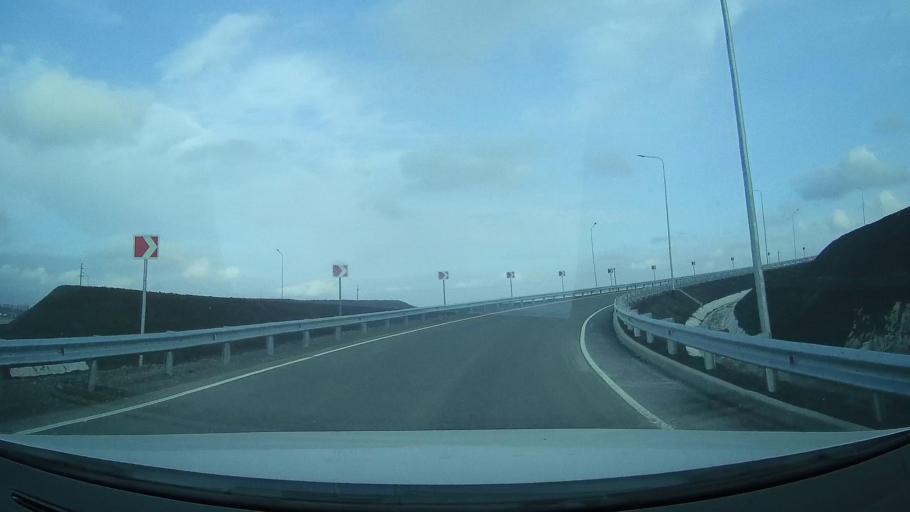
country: RU
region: Rostov
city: Grushevskaya
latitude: 47.3796
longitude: 39.8460
